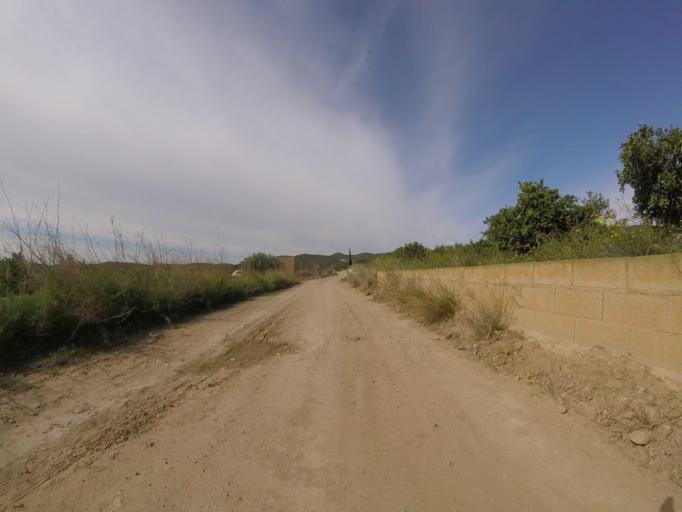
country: ES
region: Valencia
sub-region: Provincia de Castello
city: Torreblanca
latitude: 40.1984
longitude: 0.1637
